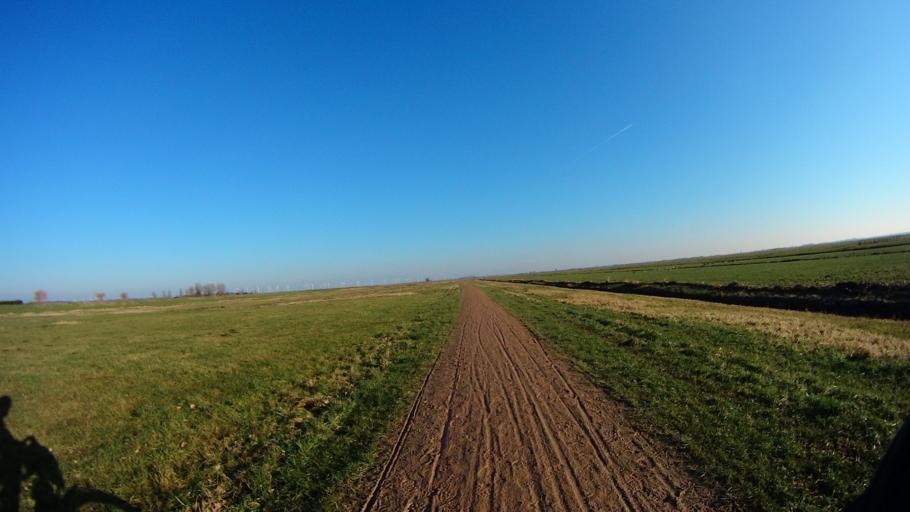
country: NL
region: North Holland
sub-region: Gemeente Blaricum
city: Blaricum
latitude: 52.2789
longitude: 5.2787
